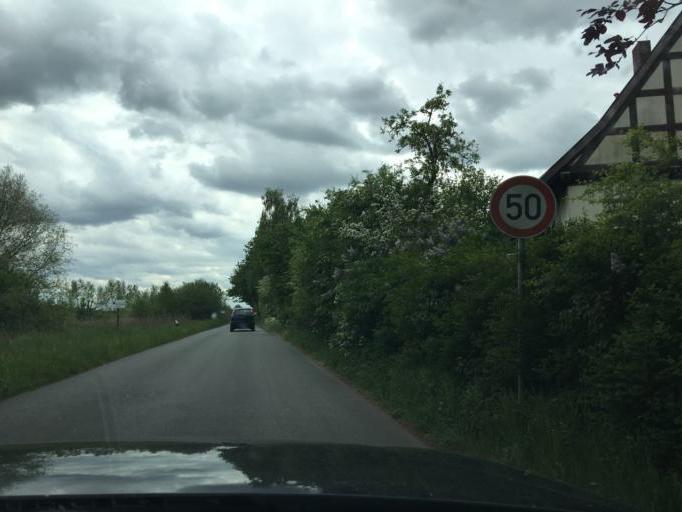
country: DE
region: North Rhine-Westphalia
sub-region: Regierungsbezirk Munster
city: Muenster
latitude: 52.0294
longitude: 7.6561
